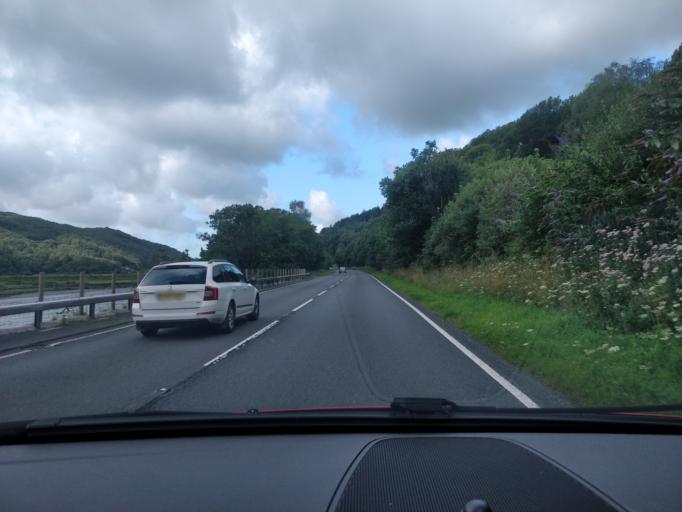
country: GB
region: Wales
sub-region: Gwynedd
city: Maentwrog
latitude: 52.9419
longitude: -4.0126
